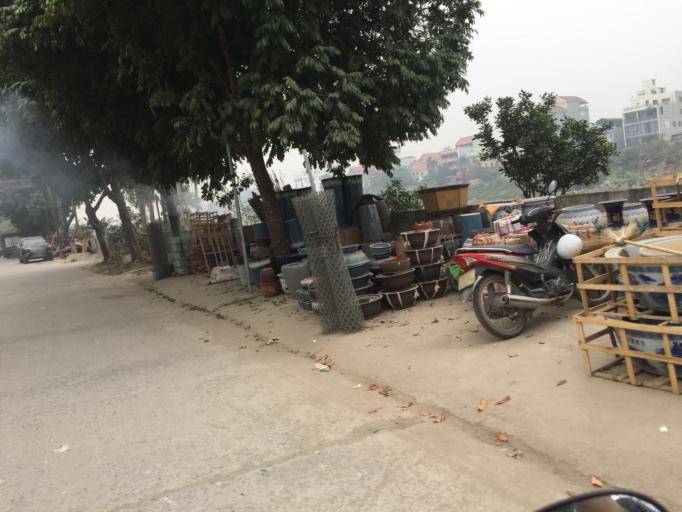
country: VN
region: Hung Yen
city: Van Giang
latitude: 20.9715
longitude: 105.9158
